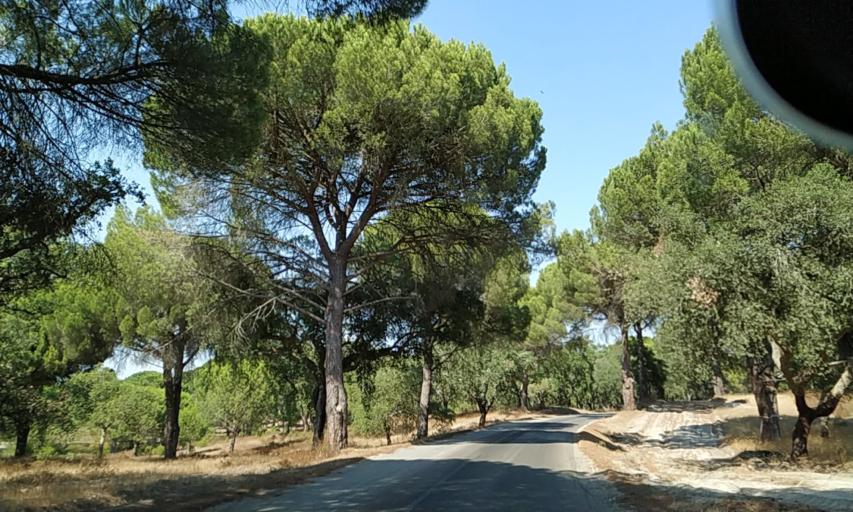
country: PT
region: Santarem
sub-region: Benavente
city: Poceirao
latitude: 38.7362
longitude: -8.6984
